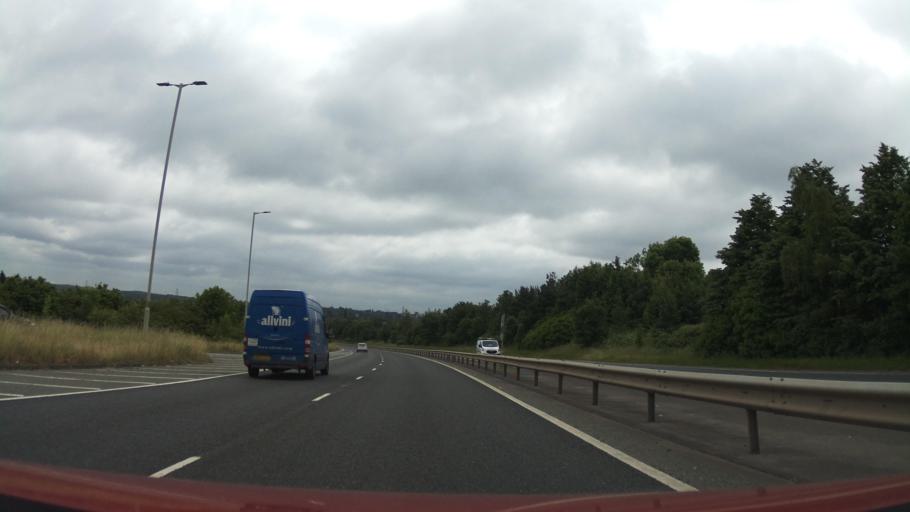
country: GB
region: England
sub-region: Leicestershire
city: Glenfield
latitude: 52.6637
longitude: -1.2224
